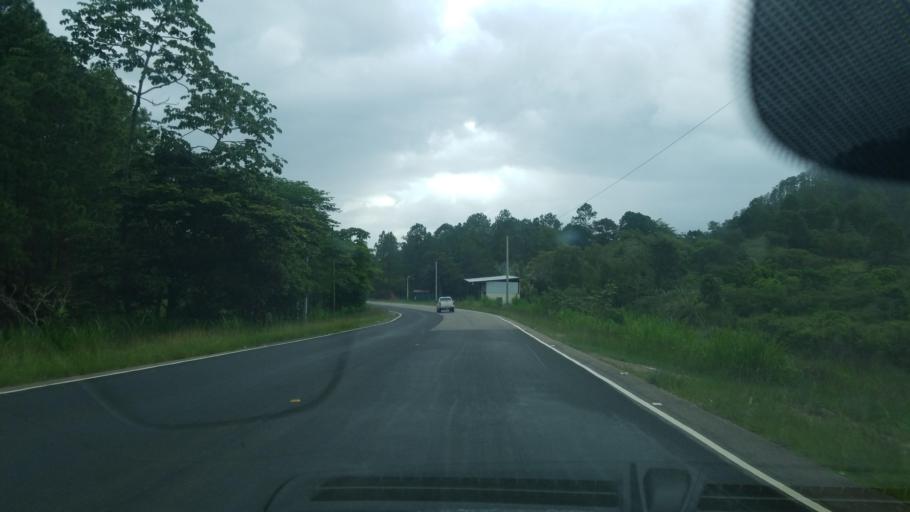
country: HN
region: Ocotepeque
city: Sinuapa
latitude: 14.4568
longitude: -89.1512
